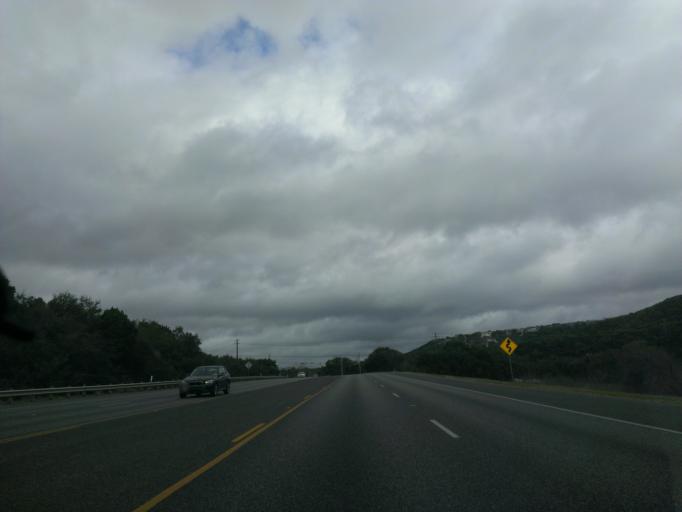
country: US
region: Texas
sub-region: Travis County
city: West Lake Hills
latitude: 30.3637
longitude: -97.7960
